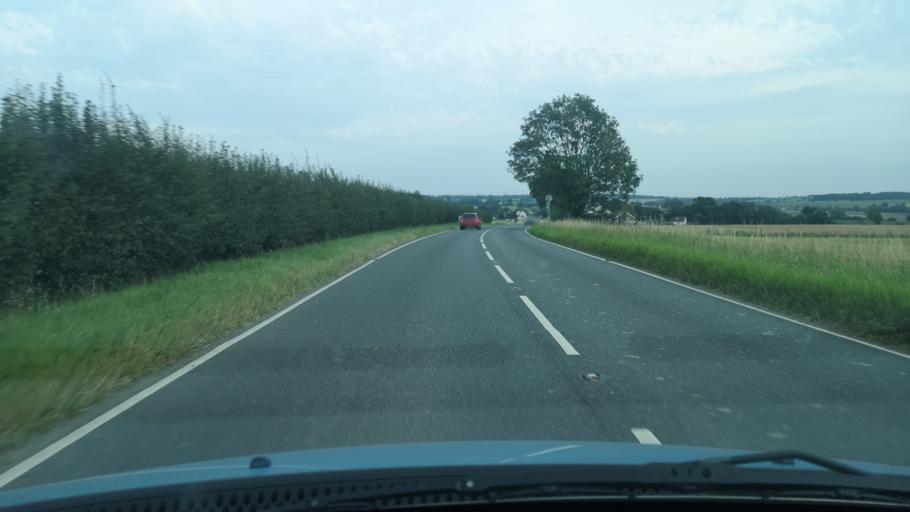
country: GB
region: England
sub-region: City and Borough of Wakefield
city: Badsworth
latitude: 53.6540
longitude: -1.2968
